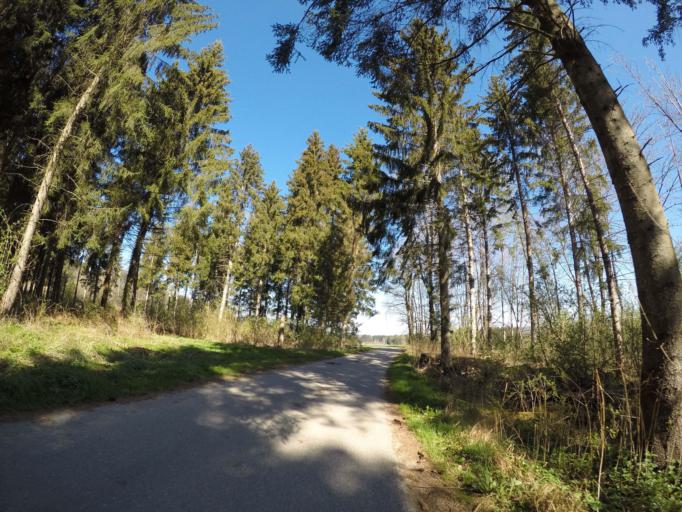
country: DE
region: Baden-Wuerttemberg
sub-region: Tuebingen Region
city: Fleischwangen
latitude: 47.8780
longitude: 9.4614
